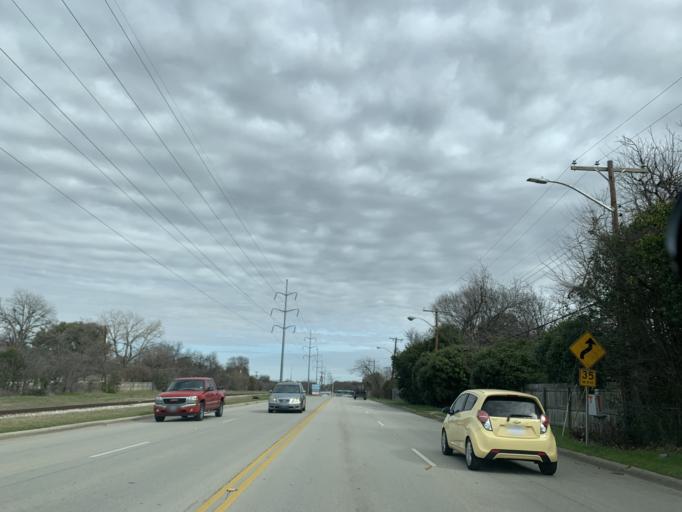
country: US
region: Texas
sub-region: Tarrant County
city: Edgecliff Village
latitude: 32.6788
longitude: -97.3763
